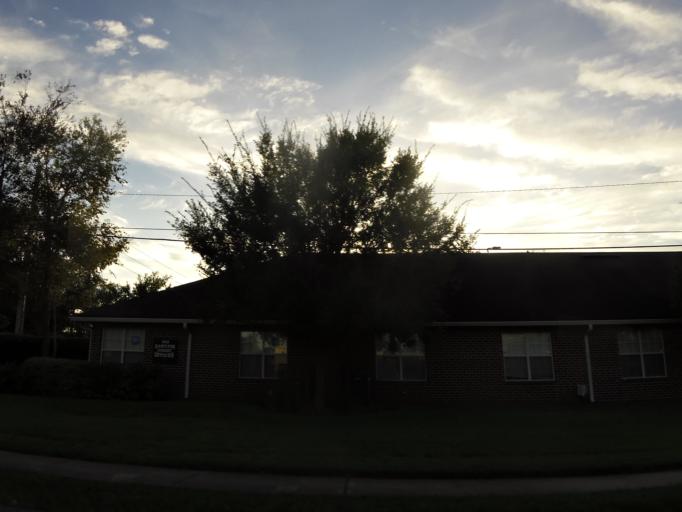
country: US
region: Florida
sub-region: Duval County
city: Jacksonville
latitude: 30.2832
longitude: -81.7220
